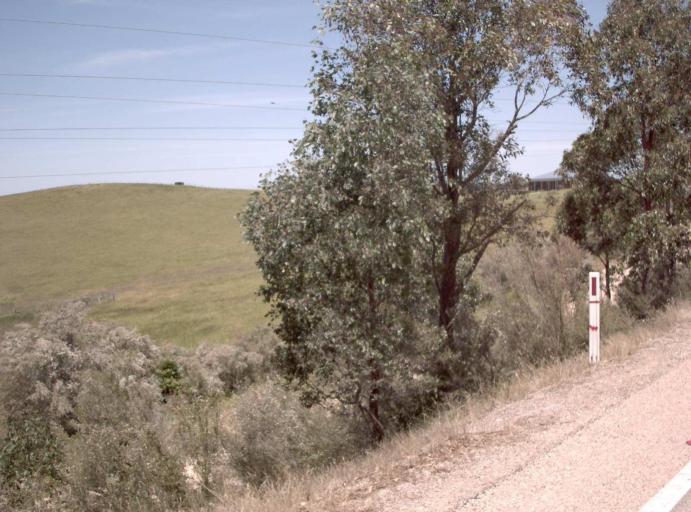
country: AU
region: Victoria
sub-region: East Gippsland
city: Bairnsdale
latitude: -37.7246
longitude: 147.8016
